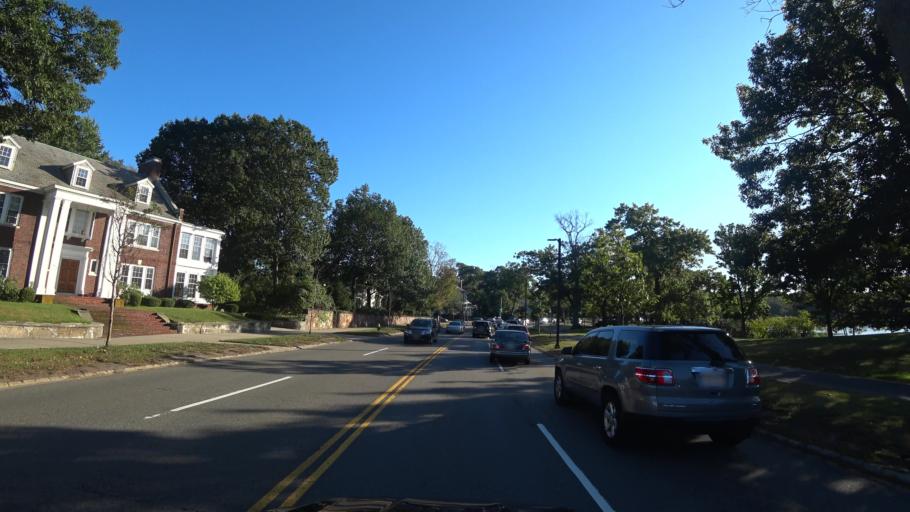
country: US
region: Massachusetts
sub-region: Suffolk County
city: Jamaica Plain
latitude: 42.3165
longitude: -71.1168
